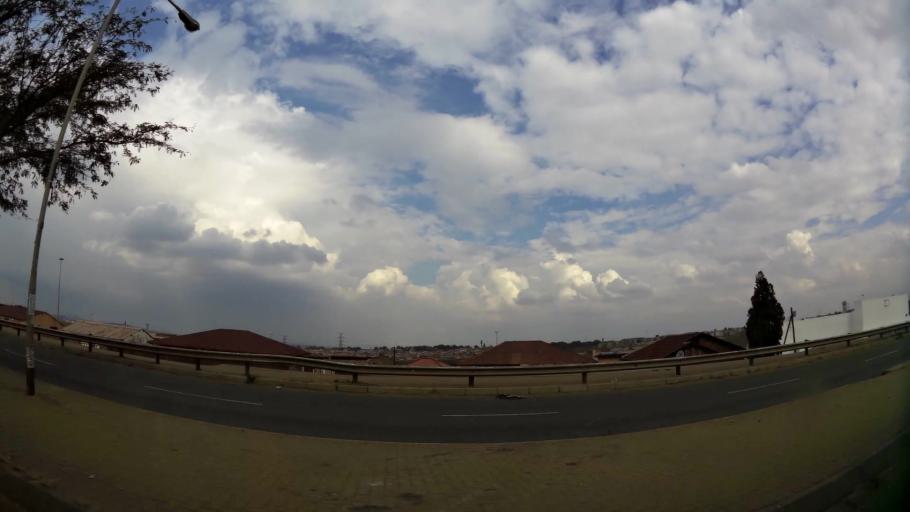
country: ZA
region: Gauteng
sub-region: City of Johannesburg Metropolitan Municipality
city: Soweto
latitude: -26.2345
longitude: 27.8687
